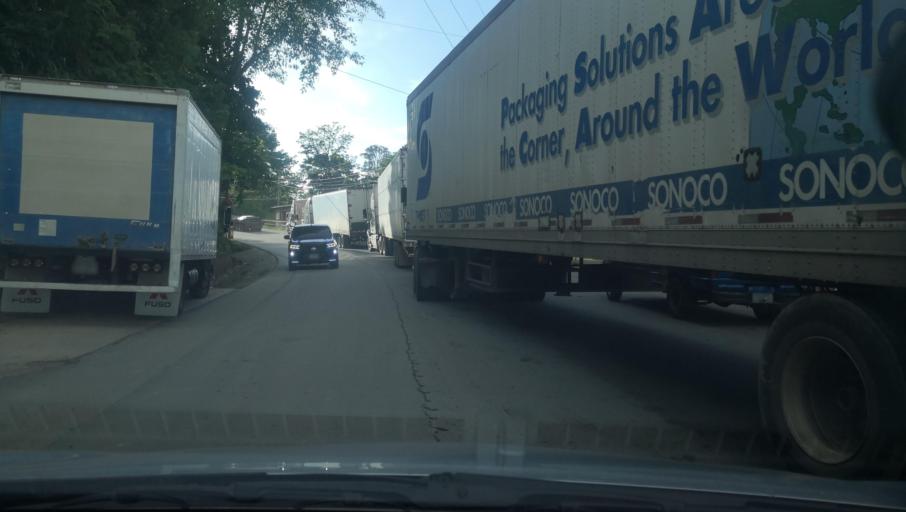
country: HN
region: El Paraiso
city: El Paraiso
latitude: 13.7902
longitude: -86.5665
